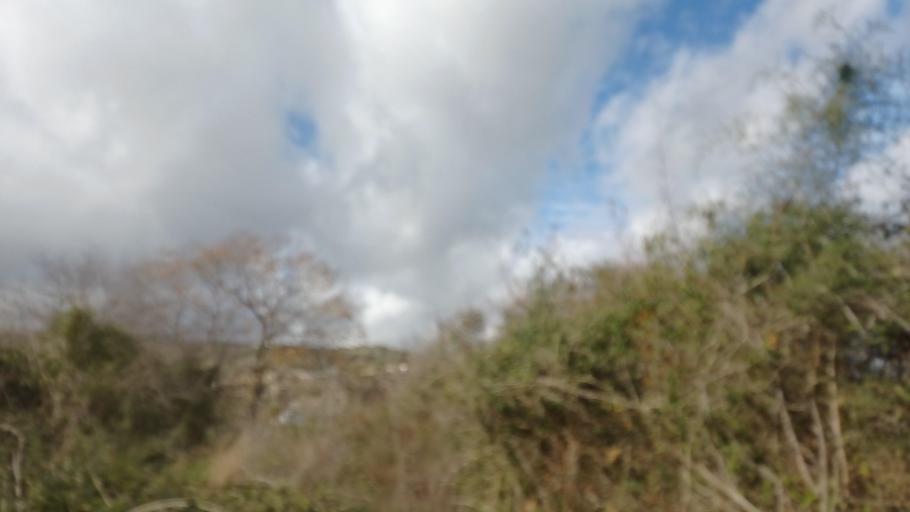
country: CY
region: Pafos
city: Polis
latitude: 34.9643
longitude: 32.4296
